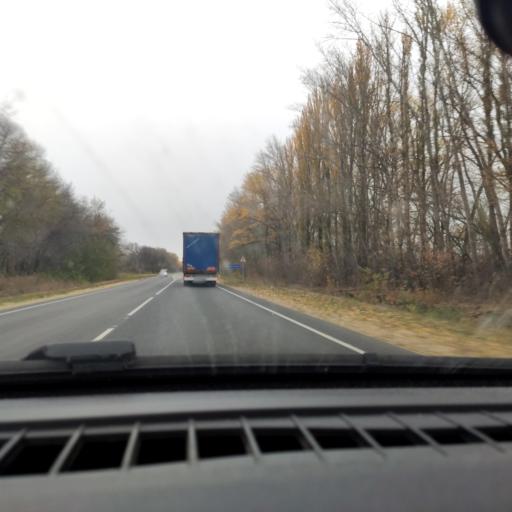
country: RU
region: Voronezj
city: Uryv-Pokrovka
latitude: 51.1791
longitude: 39.0806
